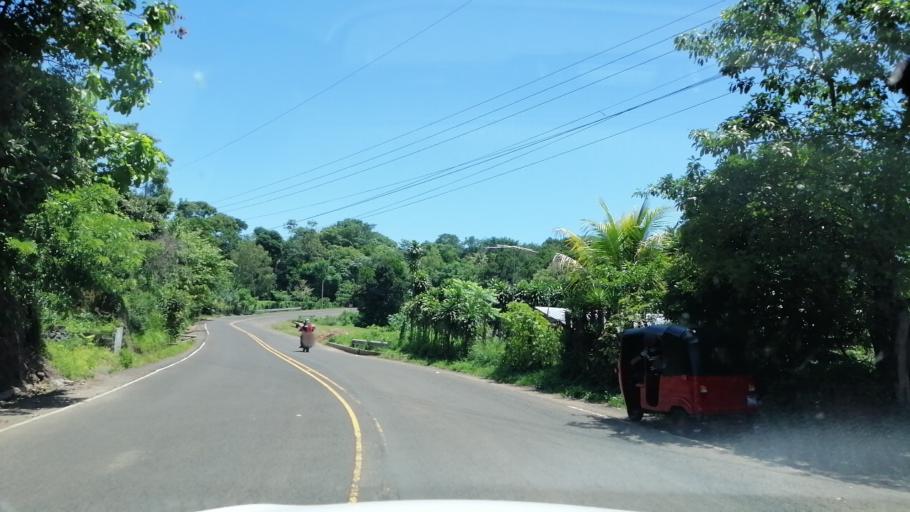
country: SV
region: San Miguel
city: Ciudad Barrios
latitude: 13.7941
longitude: -88.2855
